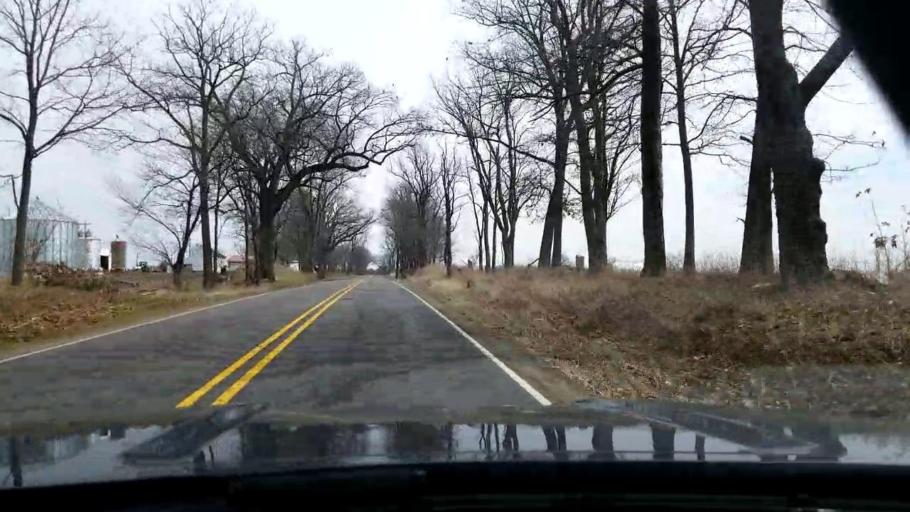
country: US
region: Michigan
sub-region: Jackson County
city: Spring Arbor
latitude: 42.1015
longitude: -84.5074
